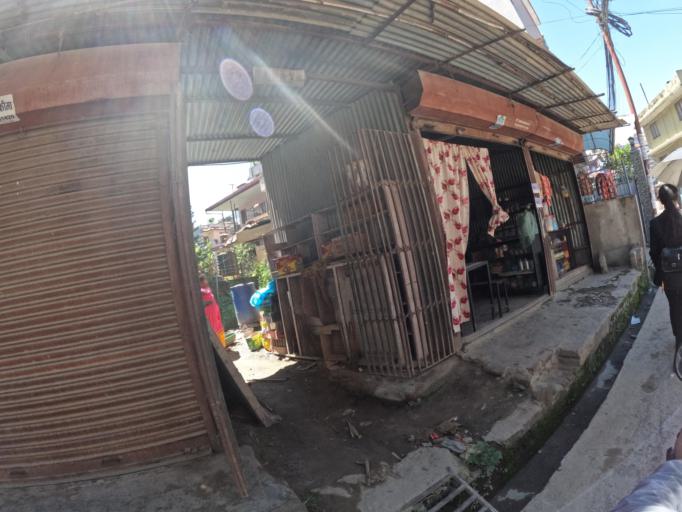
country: NP
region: Central Region
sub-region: Bagmati Zone
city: Kathmandu
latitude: 27.7404
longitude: 85.3225
